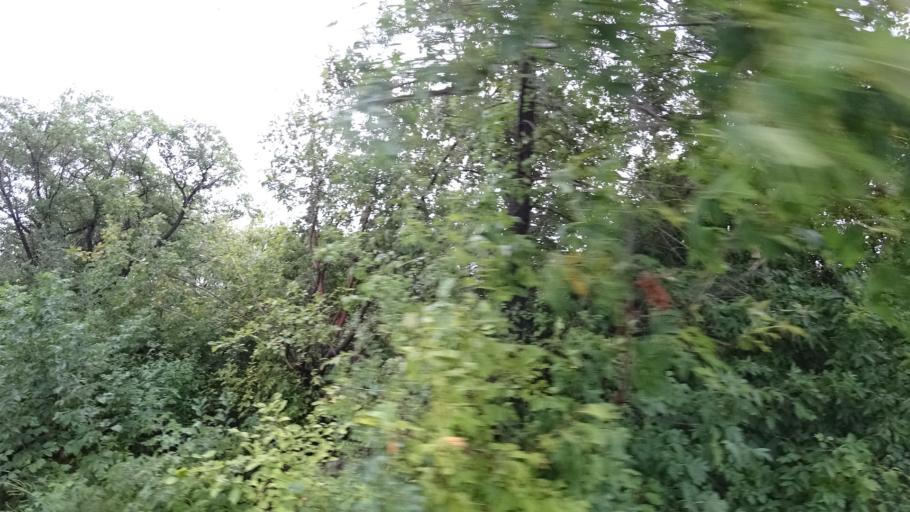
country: RU
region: Primorskiy
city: Monastyrishche
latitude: 44.2622
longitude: 132.4053
